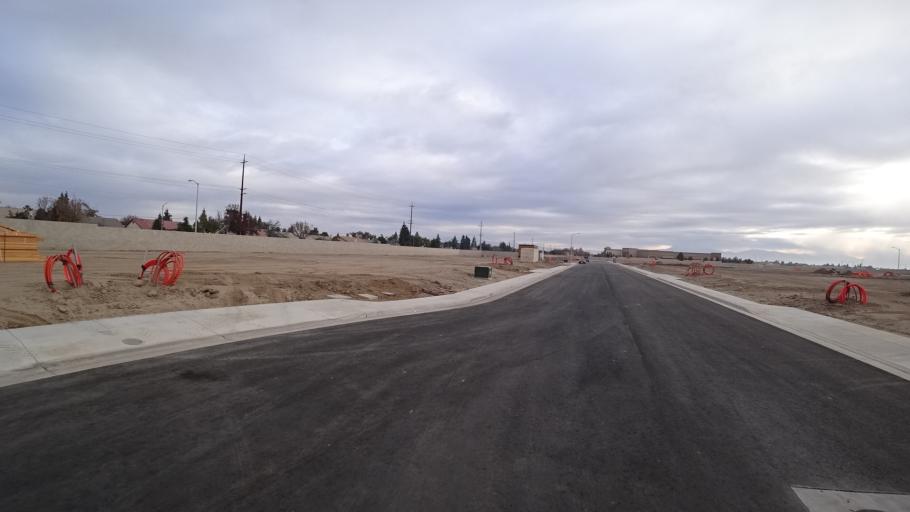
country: US
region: California
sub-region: Kern County
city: Greenfield
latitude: 35.2955
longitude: -119.0824
